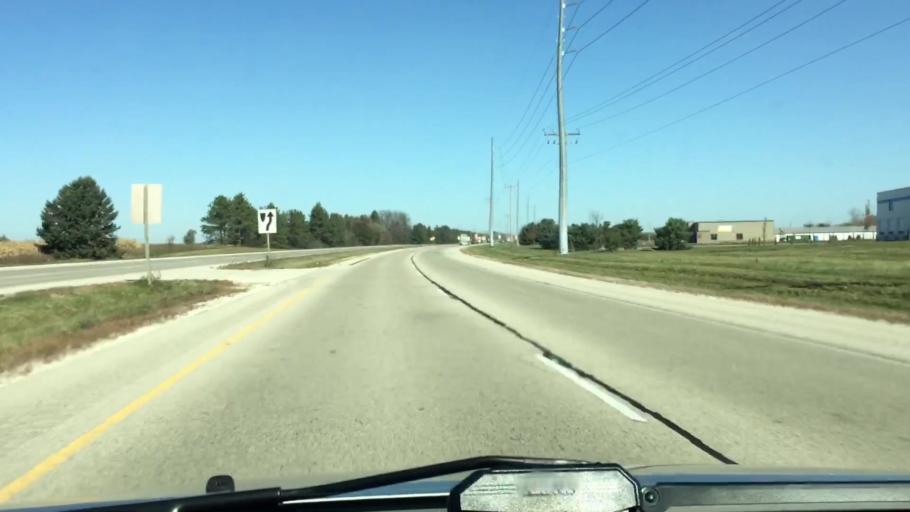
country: US
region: Wisconsin
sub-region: Waukesha County
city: Sussex
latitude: 43.1060
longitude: -88.2099
